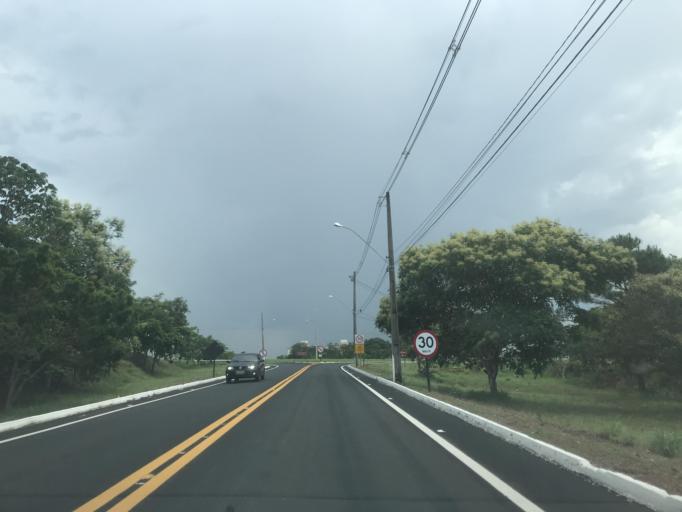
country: BR
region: Goias
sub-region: Caldas Novas
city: Caldas Novas
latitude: -17.7654
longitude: -48.7556
